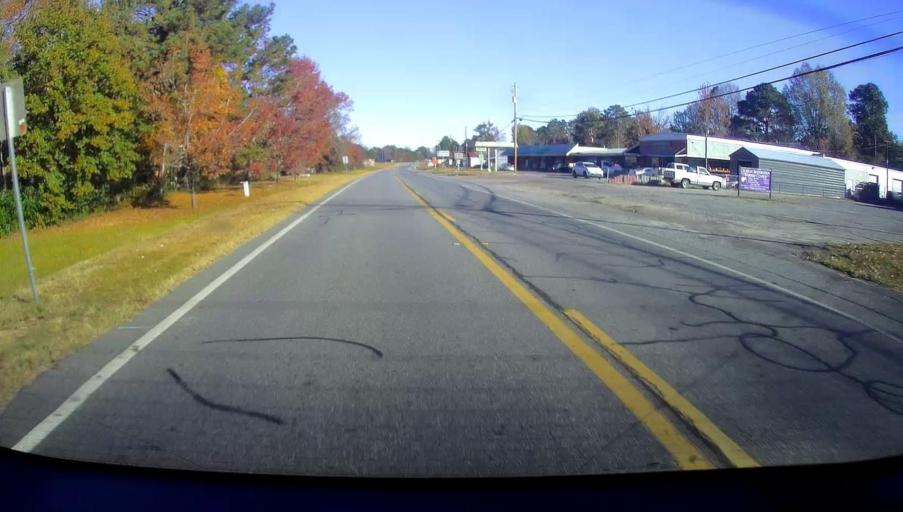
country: US
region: Georgia
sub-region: Bleckley County
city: Cochran
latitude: 32.4027
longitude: -83.3603
